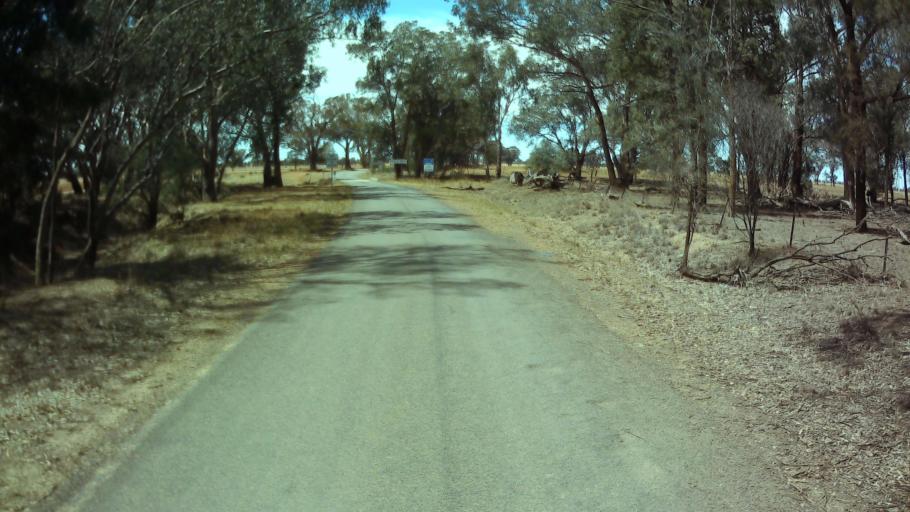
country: AU
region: New South Wales
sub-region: Weddin
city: Grenfell
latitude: -33.8595
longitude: 147.8056
